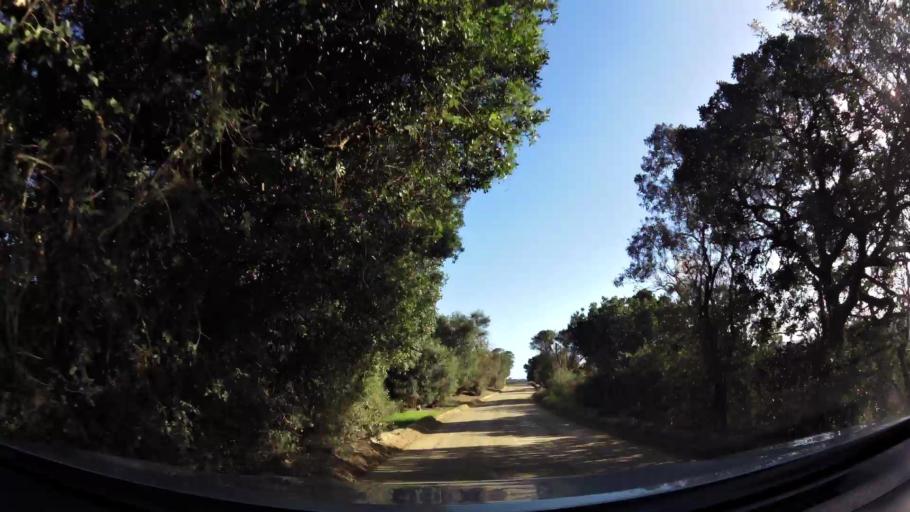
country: ZA
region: Western Cape
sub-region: Eden District Municipality
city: George
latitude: -33.9881
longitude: 22.5667
